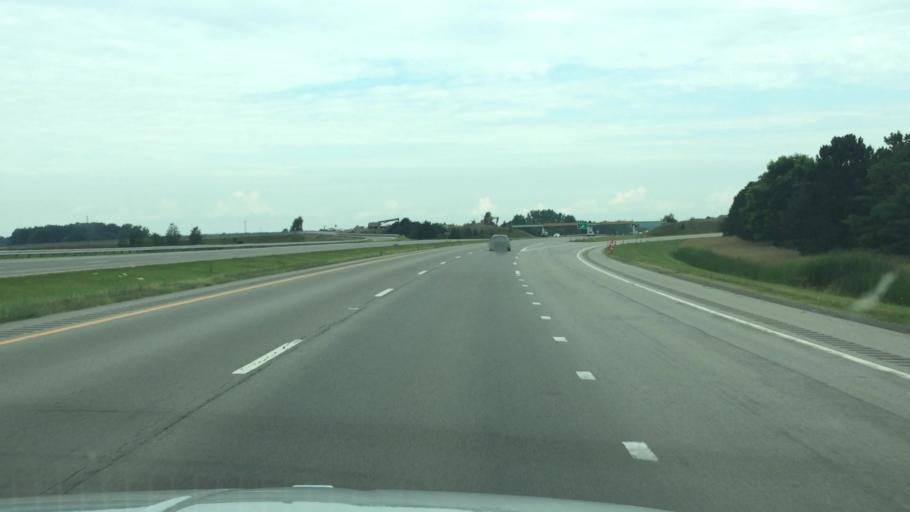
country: US
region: Ohio
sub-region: Wyandot County
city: Carey
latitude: 40.9671
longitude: -83.4808
